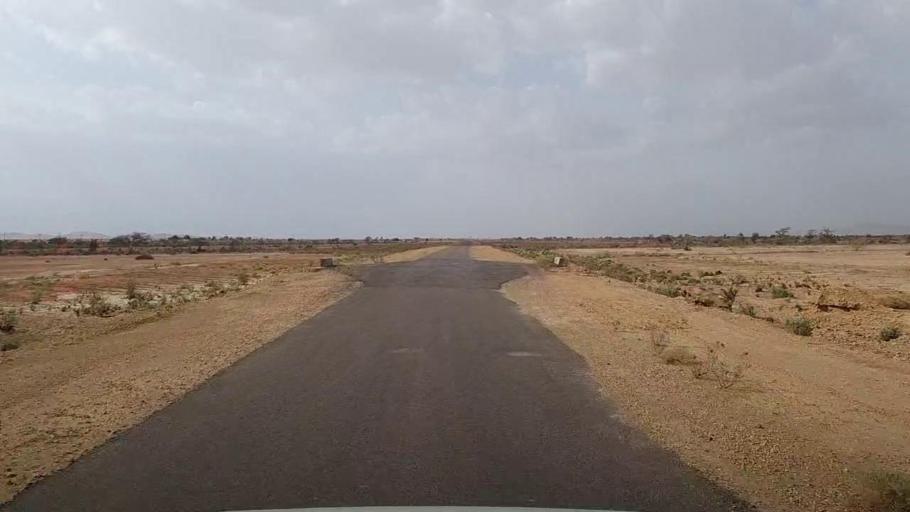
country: PK
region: Sindh
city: Jamshoro
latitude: 25.4525
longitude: 67.6779
